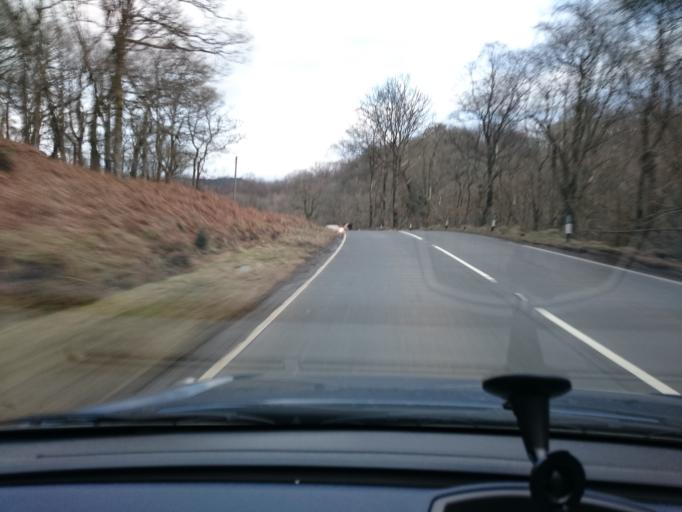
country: GB
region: Scotland
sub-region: Stirling
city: Callander
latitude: 56.2501
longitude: -4.2766
